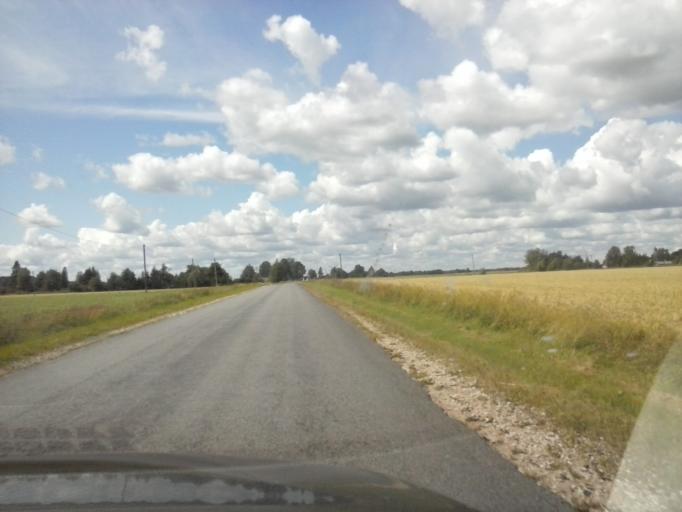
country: EE
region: Laeaene-Virumaa
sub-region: Rakke vald
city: Rakke
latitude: 59.0543
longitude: 26.3523
